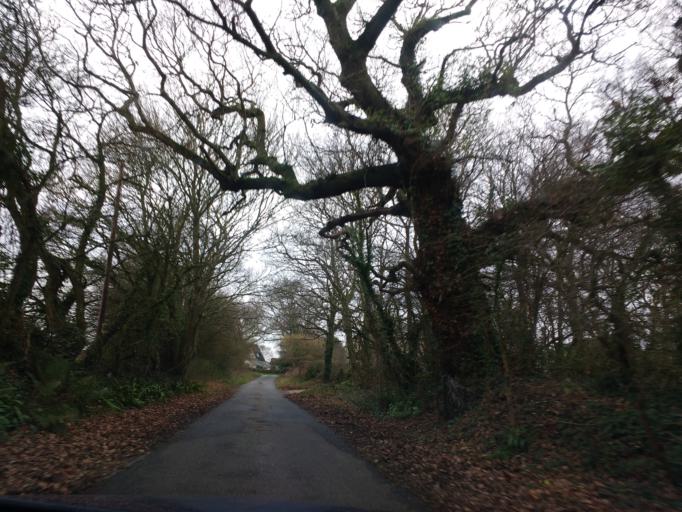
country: GB
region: England
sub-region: Isle of Wight
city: Shalfleet
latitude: 50.6904
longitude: -1.3953
